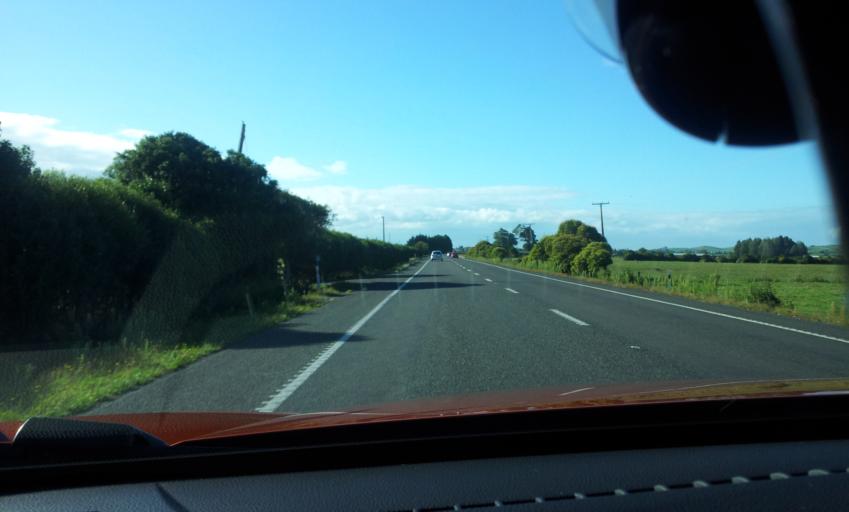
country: NZ
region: Waikato
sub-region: Hauraki District
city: Ngatea
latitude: -37.4039
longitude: 175.4727
